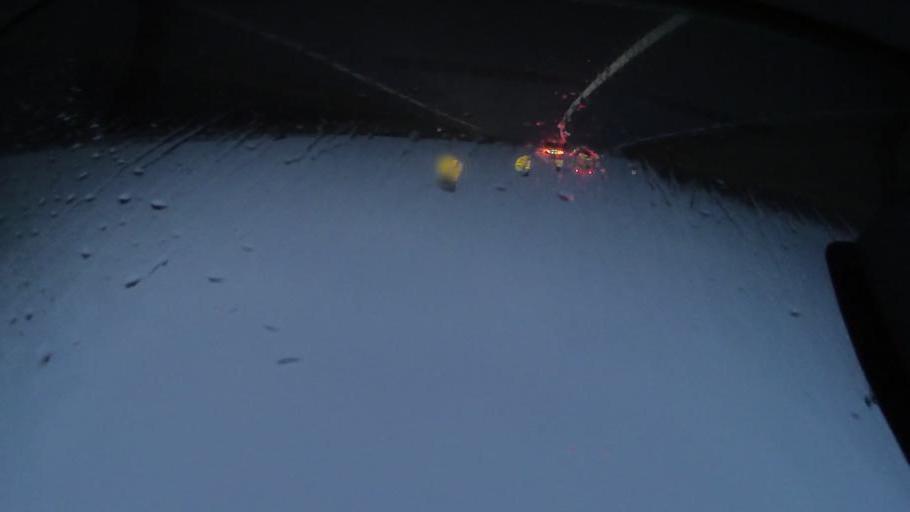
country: RO
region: Harghita
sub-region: Comuna Ditrau
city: Ditrau
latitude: 46.8212
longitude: 25.4923
